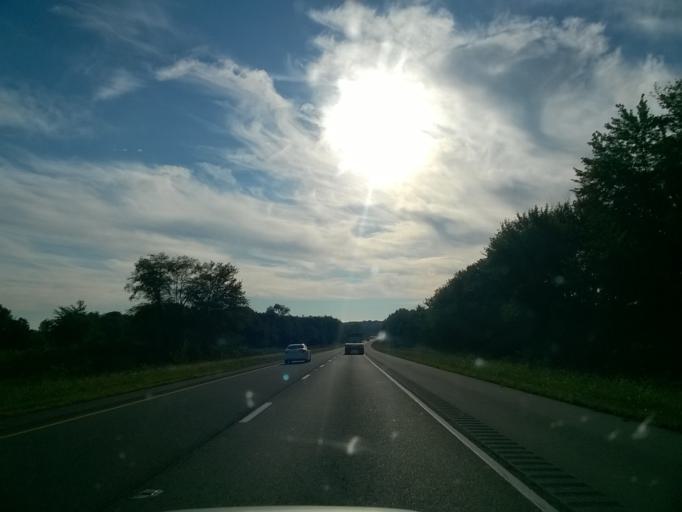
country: US
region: Indiana
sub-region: Spencer County
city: Dale
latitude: 38.1974
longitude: -87.1487
